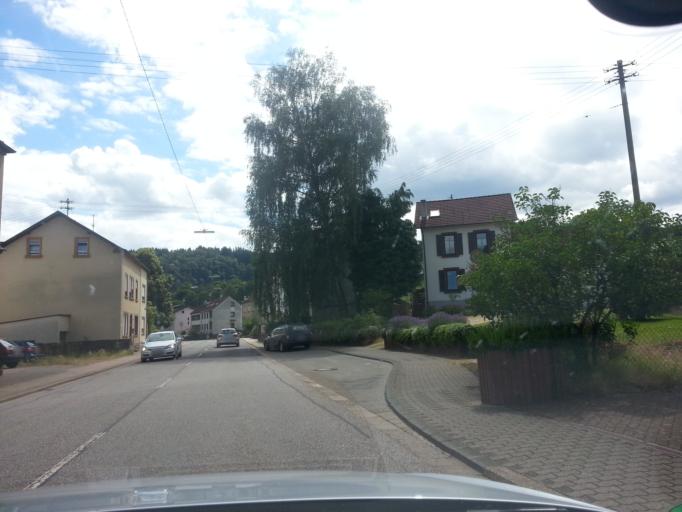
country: DE
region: Saarland
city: Mettlach
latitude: 49.4976
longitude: 6.5864
